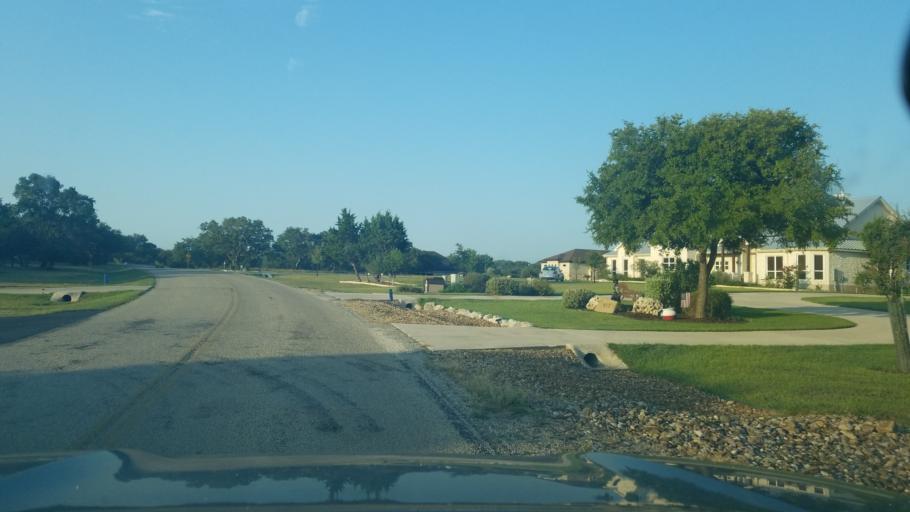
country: US
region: Texas
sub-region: Comal County
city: Bulverde
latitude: 29.8384
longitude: -98.4058
